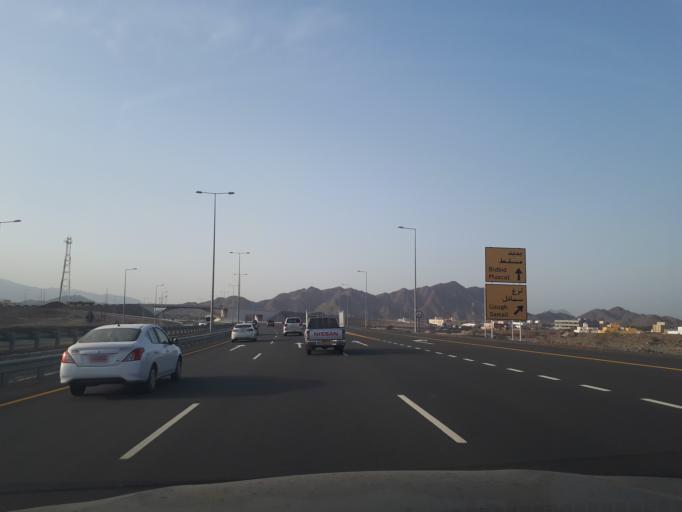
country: OM
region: Muhafazat ad Dakhiliyah
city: Bidbid
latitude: 23.3246
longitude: 58.1159
